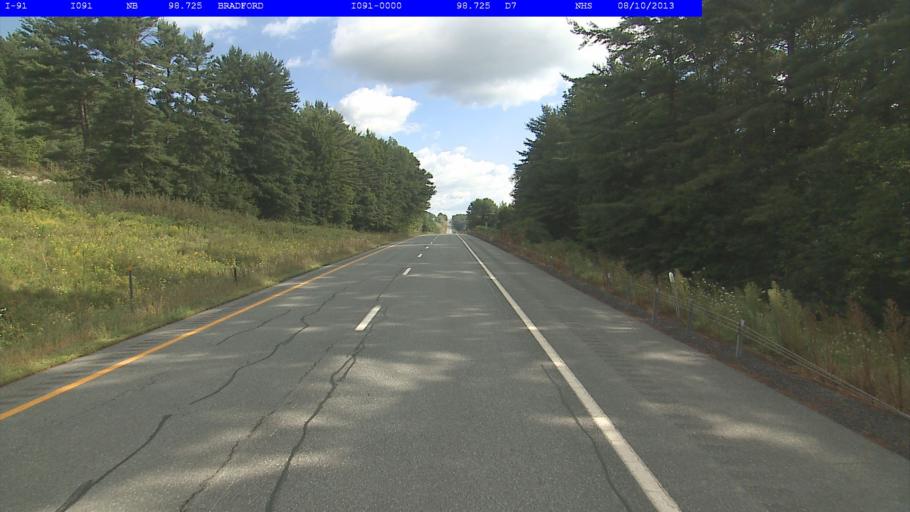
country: US
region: New Hampshire
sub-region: Grafton County
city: Haverhill
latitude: 43.9980
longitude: -72.1307
